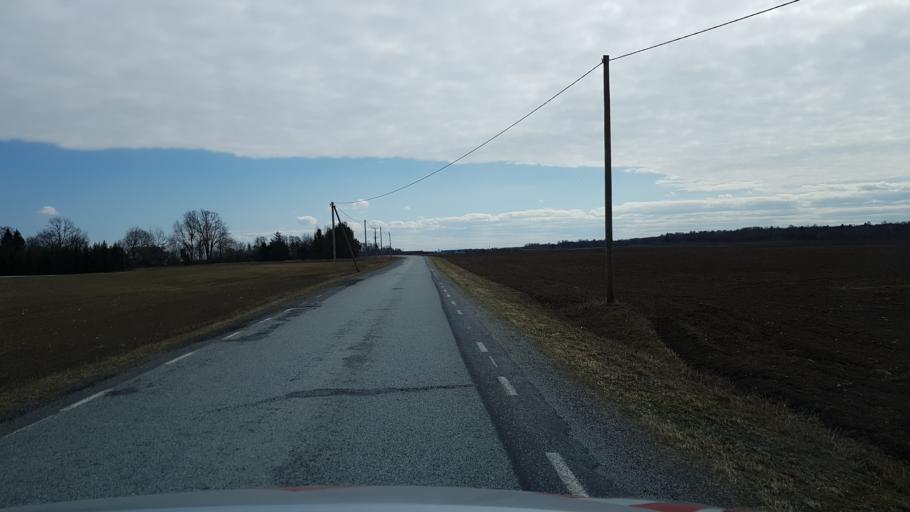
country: EE
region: Laeaene-Virumaa
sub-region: Haljala vald
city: Haljala
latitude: 59.4281
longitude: 26.2149
